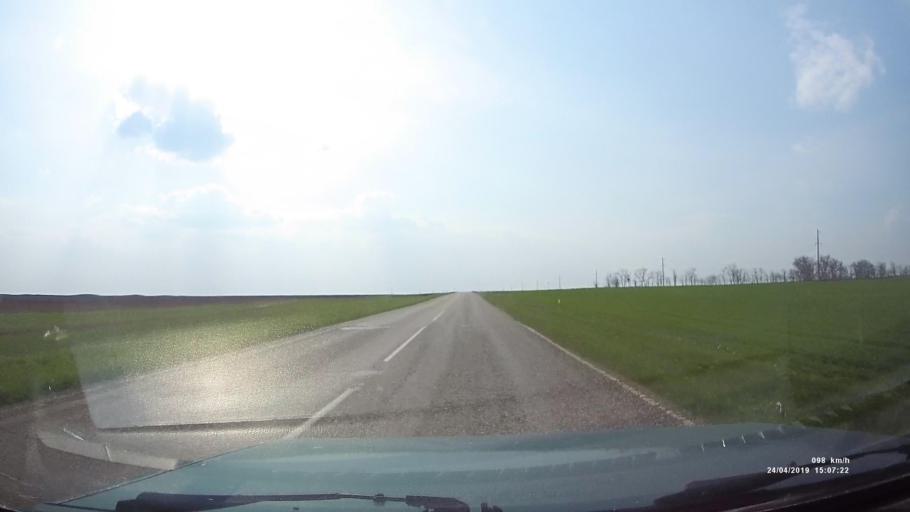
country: RU
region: Rostov
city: Remontnoye
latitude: 46.5597
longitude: 43.4065
